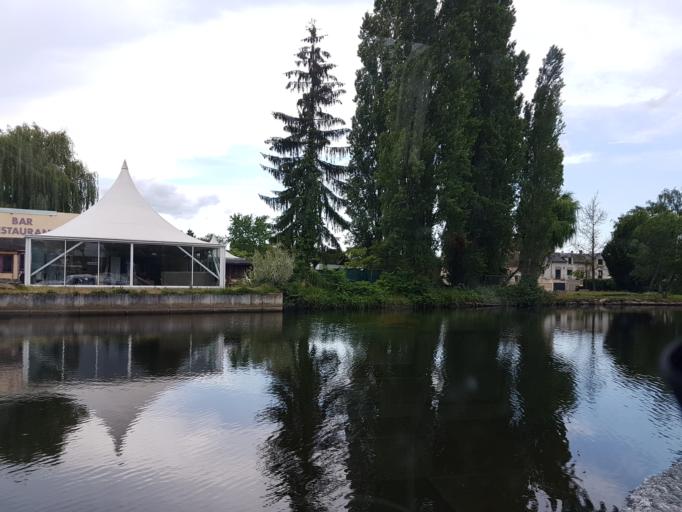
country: FR
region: Bourgogne
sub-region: Departement de l'Yonne
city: Moneteau
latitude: 47.8480
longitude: 3.5785
